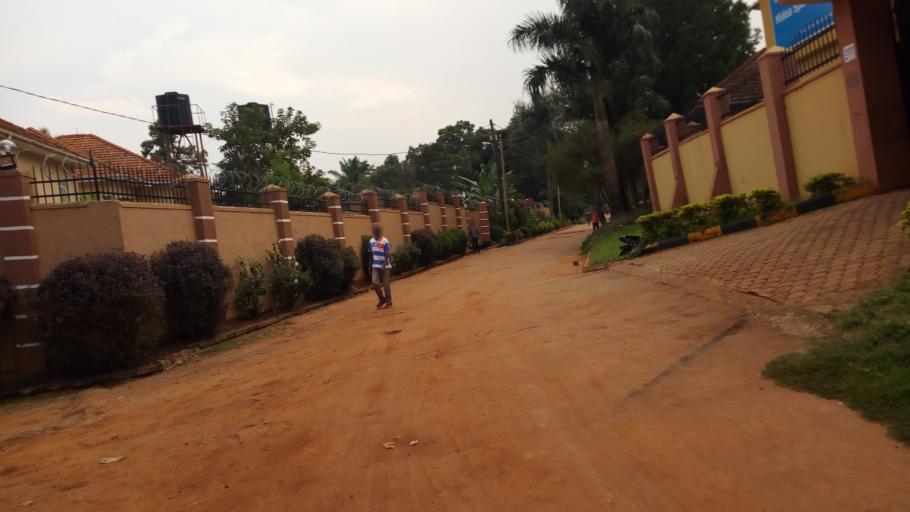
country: UG
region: Central Region
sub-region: Wakiso District
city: Kireka
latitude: 0.3210
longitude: 32.6309
